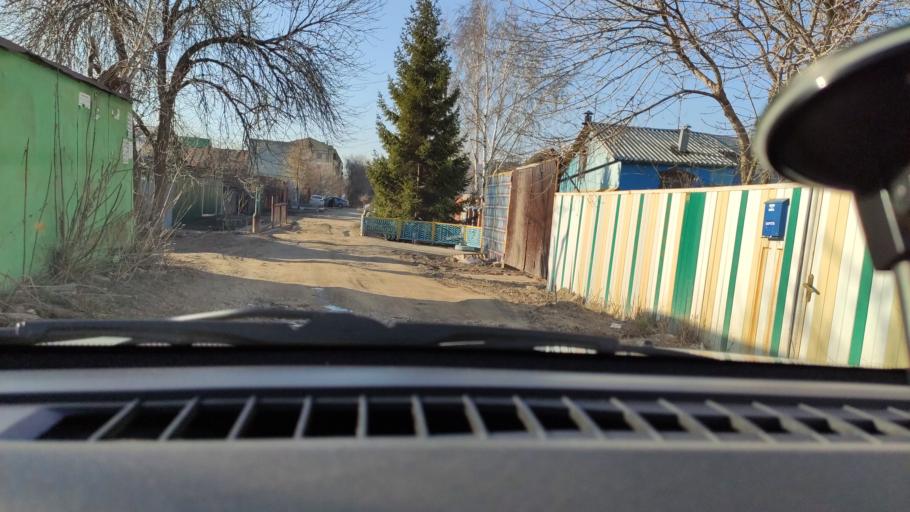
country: RU
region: Samara
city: Samara
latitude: 53.2040
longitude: 50.2068
